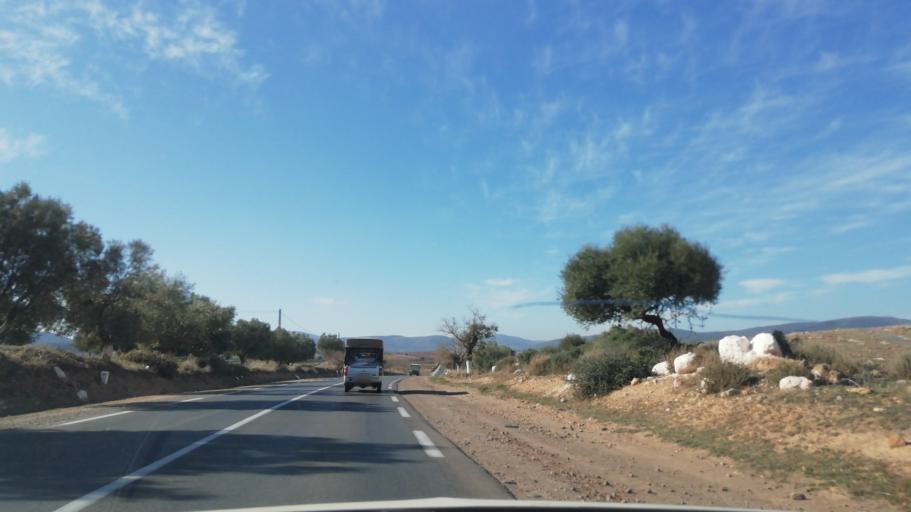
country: DZ
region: Tlemcen
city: Ouled Mimoun
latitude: 34.8798
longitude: -1.0947
